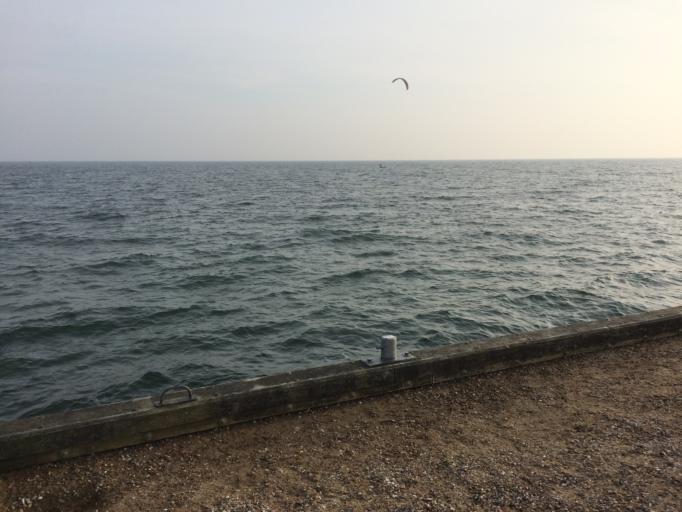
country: DK
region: Zealand
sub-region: Odsherred Kommune
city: Nykobing Sjaelland
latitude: 55.9440
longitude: 11.7691
